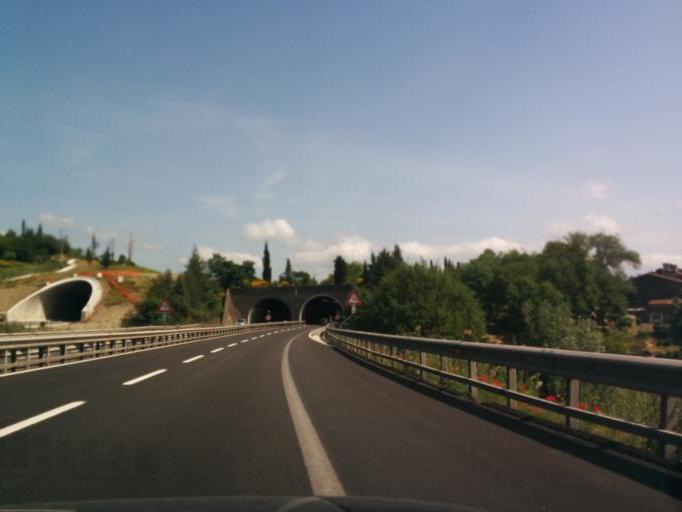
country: IT
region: Tuscany
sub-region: Province of Florence
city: Cavallina
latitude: 43.9587
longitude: 11.2090
